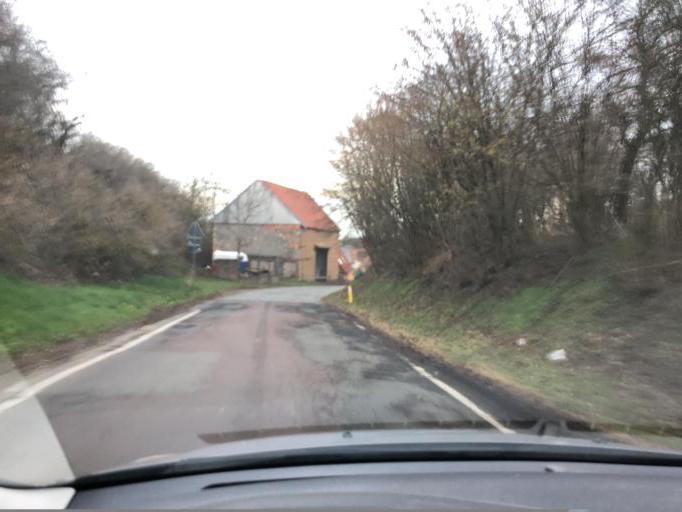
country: DE
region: Saxony-Anhalt
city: Laucha
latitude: 51.2050
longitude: 11.6796
